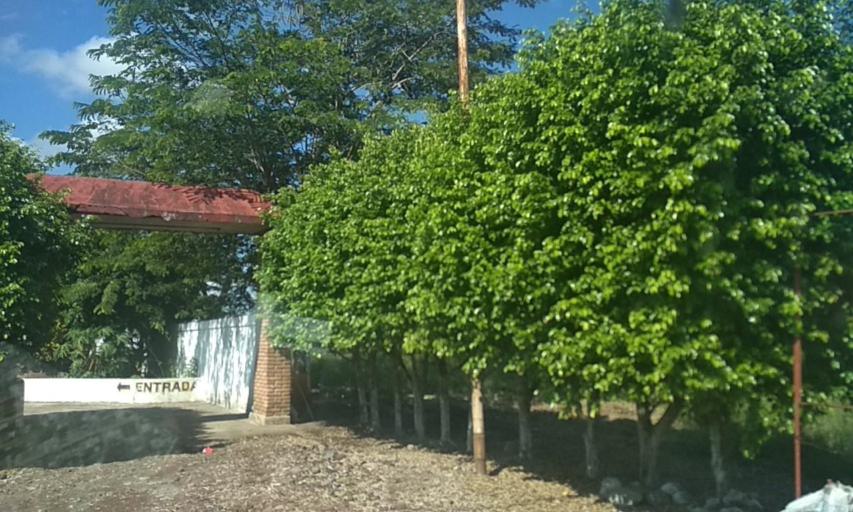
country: MX
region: Veracruz
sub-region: Martinez de la Torre
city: La Union Paso Largo
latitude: 20.1338
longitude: -96.9973
